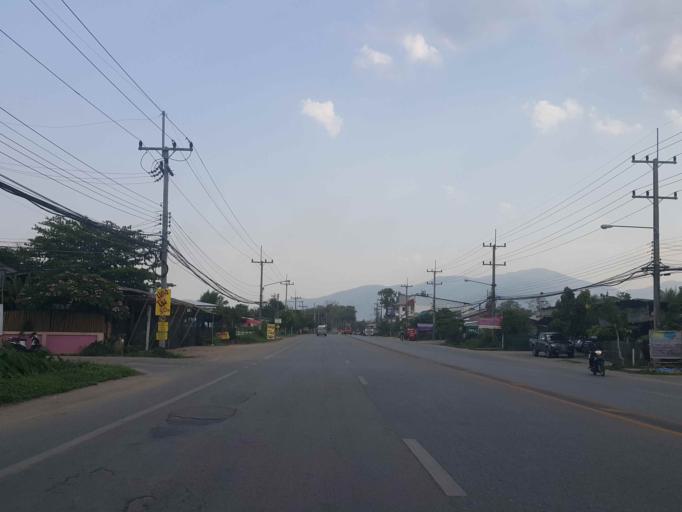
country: TH
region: Chiang Mai
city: San Sai
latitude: 18.9510
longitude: 98.9445
